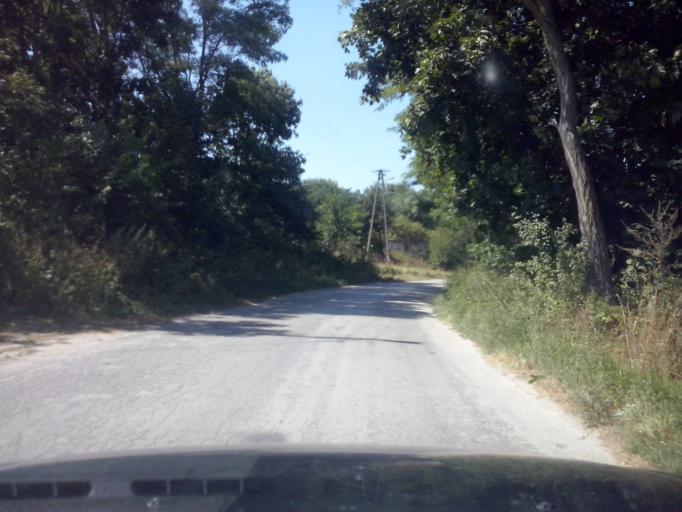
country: PL
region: Swietokrzyskie
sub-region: Powiat kielecki
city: Chmielnik
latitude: 50.6035
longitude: 20.7890
